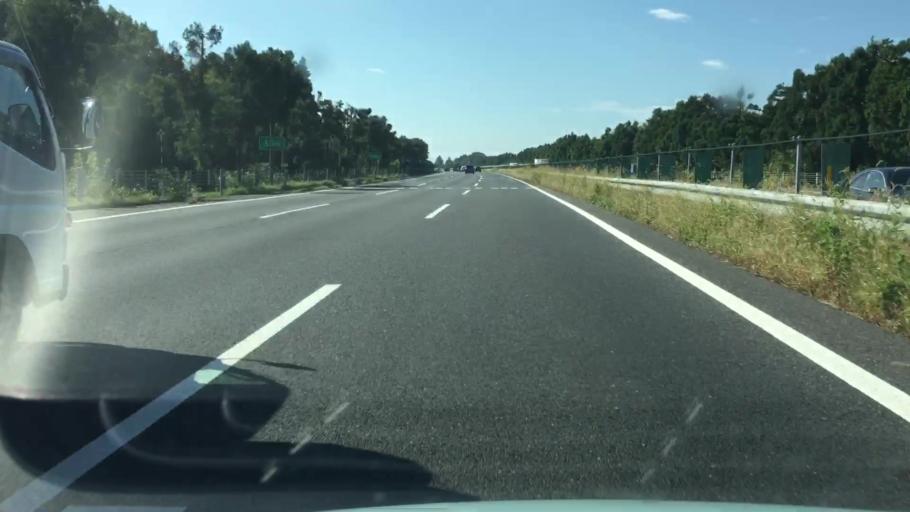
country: JP
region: Ibaraki
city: Tomobe
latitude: 36.2636
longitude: 140.3003
